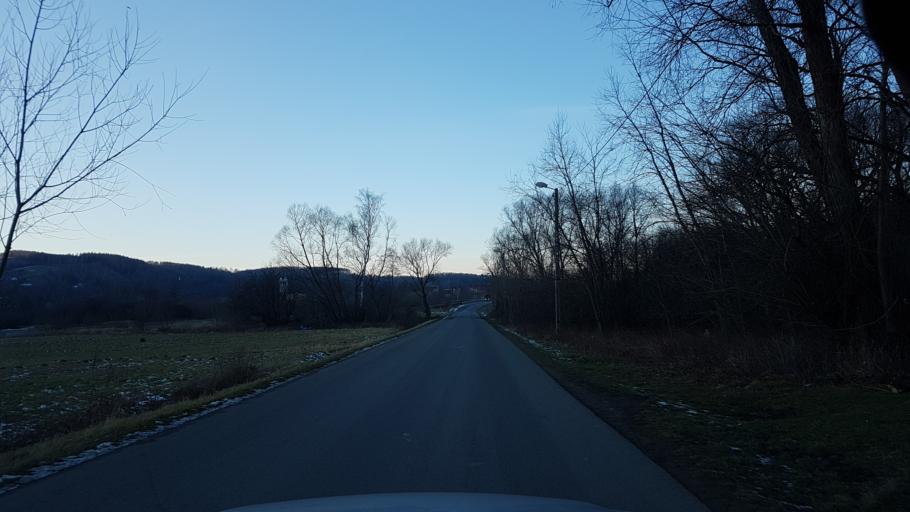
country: PL
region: Lesser Poland Voivodeship
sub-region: Powiat nowosadecki
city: Rytro
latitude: 49.5220
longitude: 20.6597
